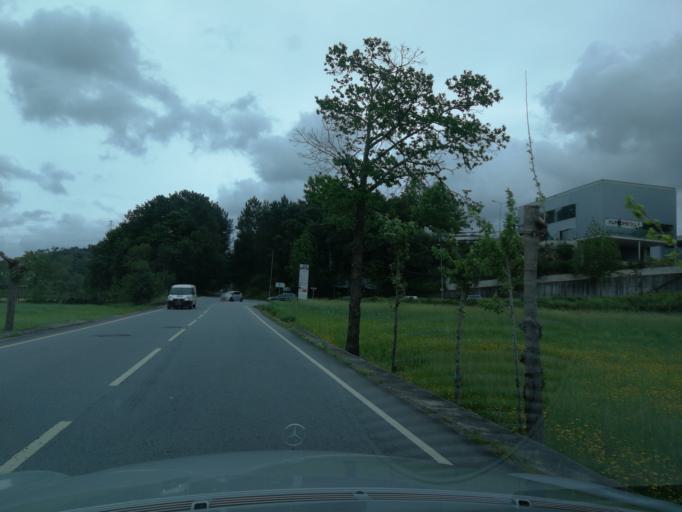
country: PT
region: Braga
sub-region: Braga
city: Adaufe
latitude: 41.6017
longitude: -8.4146
